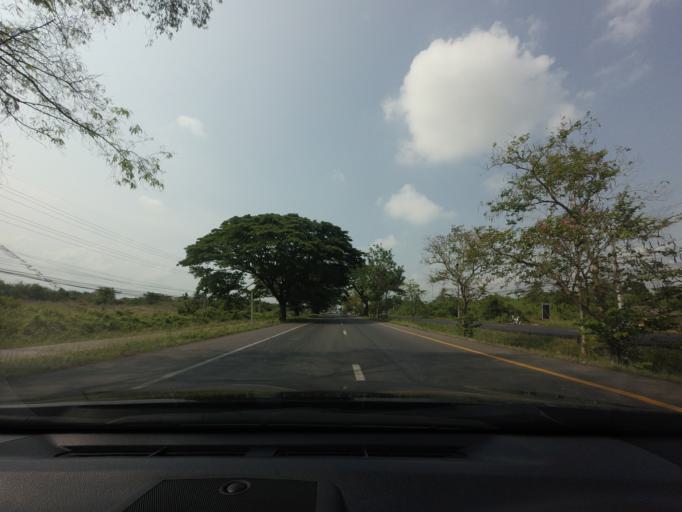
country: TH
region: Prachuap Khiri Khan
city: Sam Roi Yot
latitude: 12.2770
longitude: 99.8717
